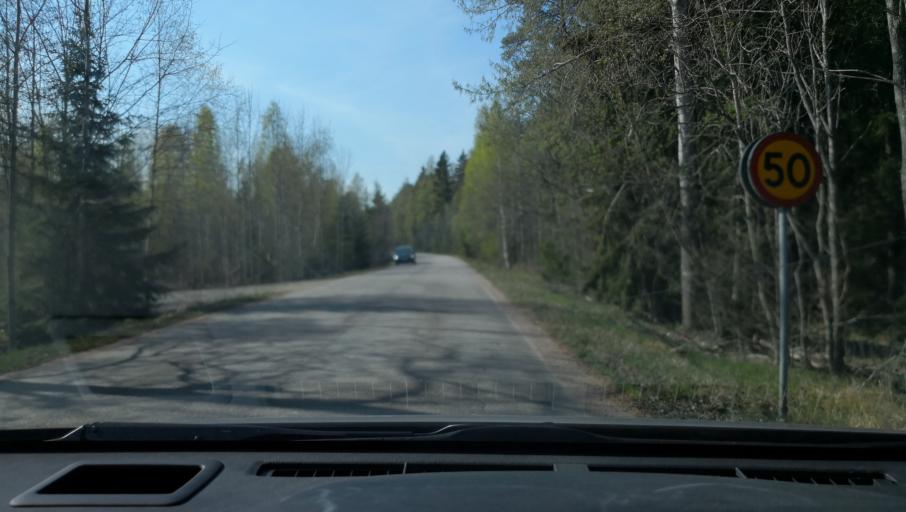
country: SE
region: Uppsala
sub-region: Heby Kommun
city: Tarnsjo
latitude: 60.2646
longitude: 16.9254
